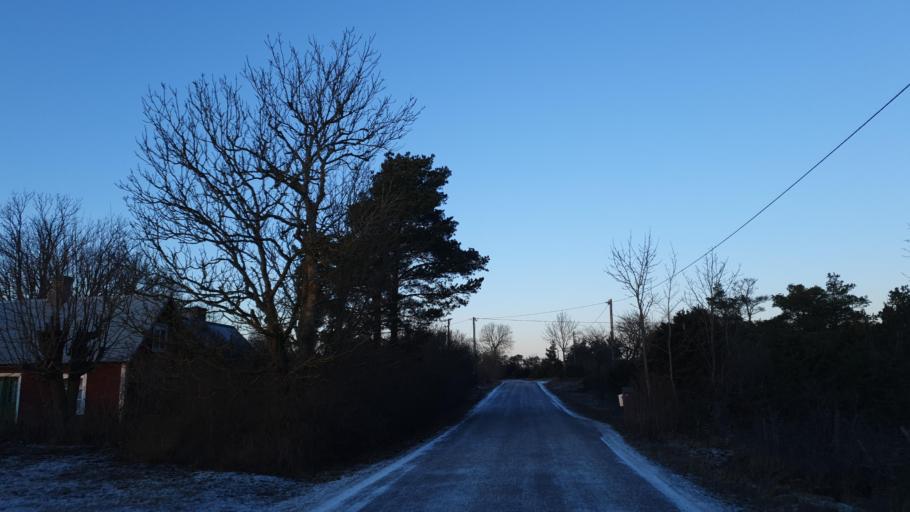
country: SE
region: Gotland
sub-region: Gotland
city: Slite
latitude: 57.3896
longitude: 18.8089
